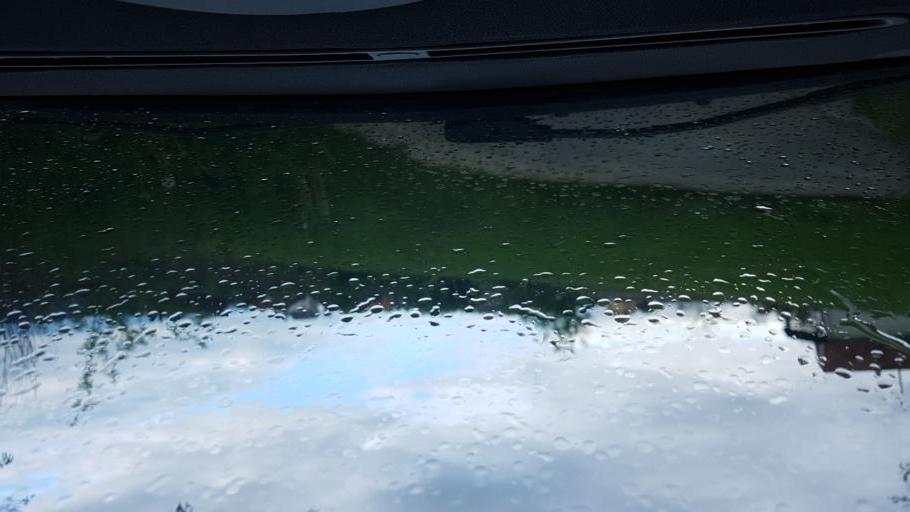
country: HR
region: Krapinsko-Zagorska
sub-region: Grad Krapina
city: Krapina
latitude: 46.1687
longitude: 15.8176
